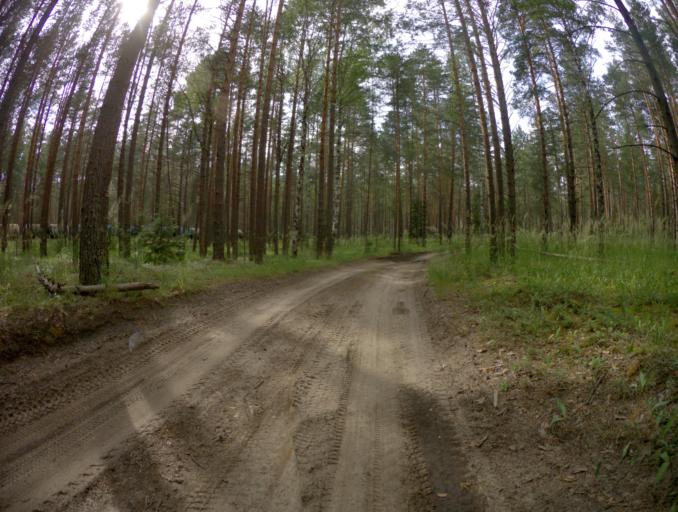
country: RU
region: Nizjnij Novgorod
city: Frolishchi
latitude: 56.3123
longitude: 42.6585
